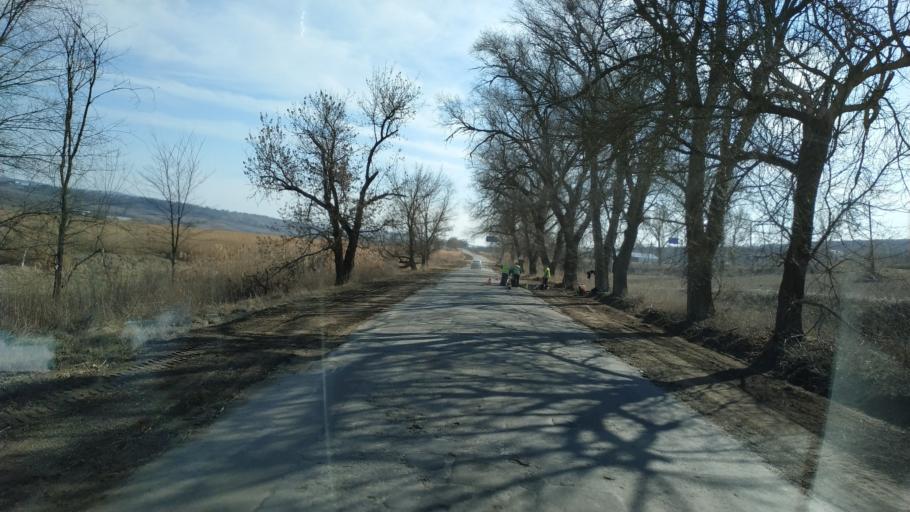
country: MD
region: Nisporeni
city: Nisporeni
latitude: 47.0900
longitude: 28.1373
